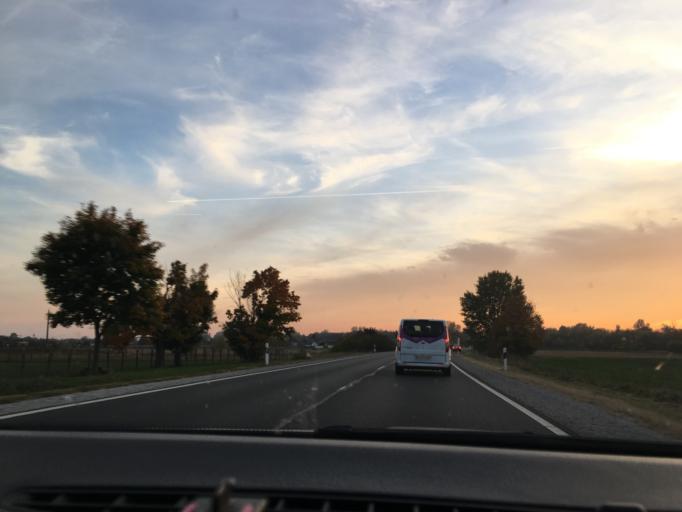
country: HU
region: Hajdu-Bihar
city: Teglas
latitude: 47.7252
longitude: 21.6758
